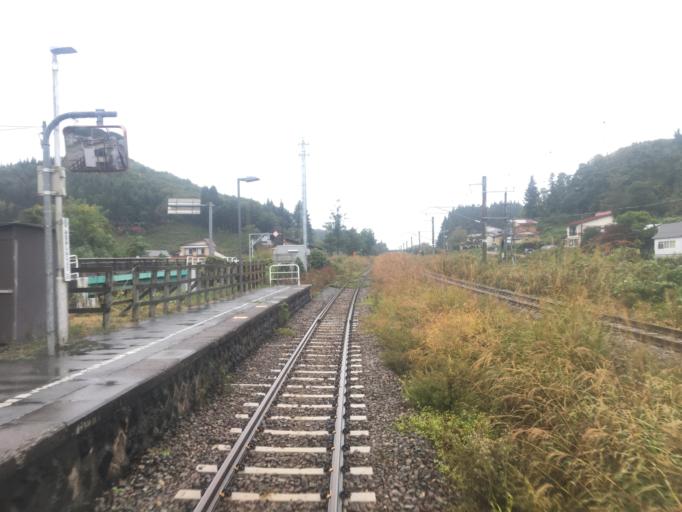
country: JP
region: Yamagata
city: Shinjo
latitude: 38.7212
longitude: 140.3169
